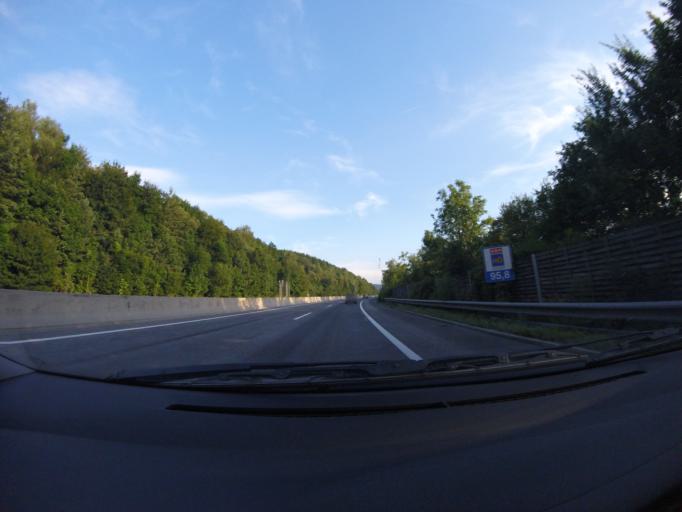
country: AT
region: Lower Austria
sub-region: Politischer Bezirk Neunkirchen
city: Grimmenstein
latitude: 47.6226
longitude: 16.1332
